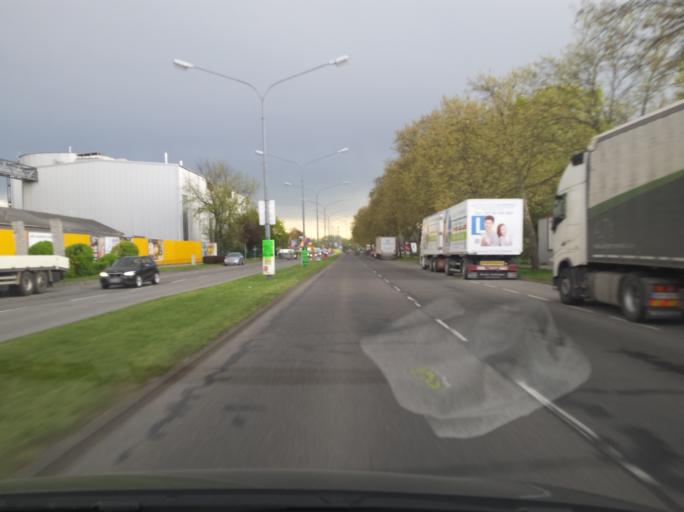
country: AT
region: Lower Austria
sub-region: Politischer Bezirk Wien-Umgebung
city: Gerasdorf bei Wien
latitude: 48.2248
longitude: 16.4446
